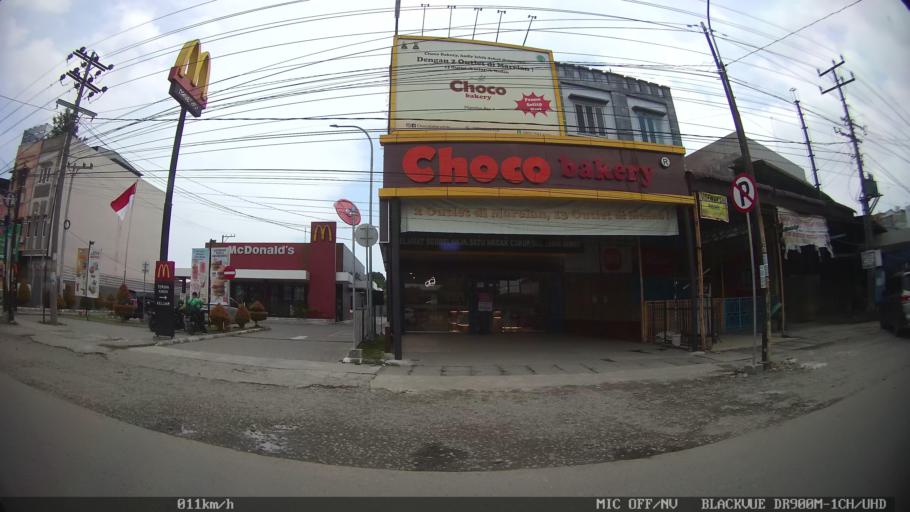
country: ID
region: North Sumatra
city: Labuhan Deli
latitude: 3.6900
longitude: 98.6563
